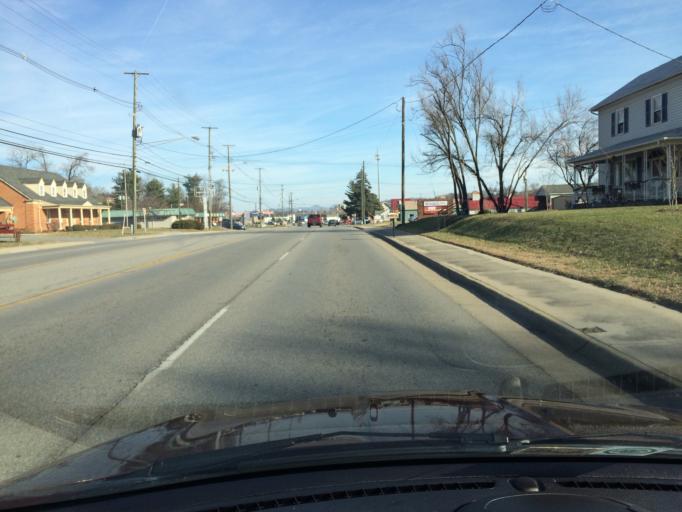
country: US
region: Virginia
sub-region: City of Salem
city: Salem
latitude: 37.2815
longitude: -80.1099
